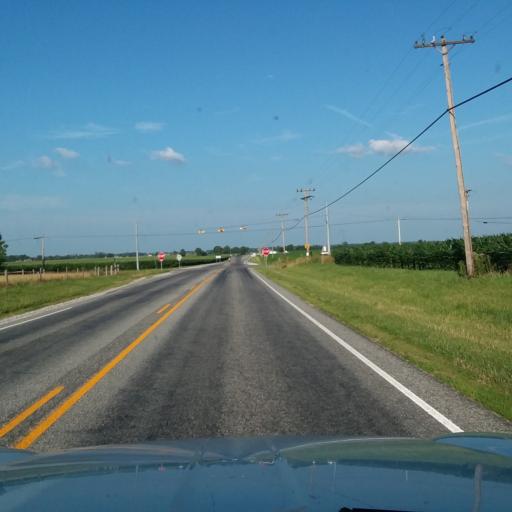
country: US
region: Indiana
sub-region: Johnson County
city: Princes Lakes
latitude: 39.4102
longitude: -86.0869
